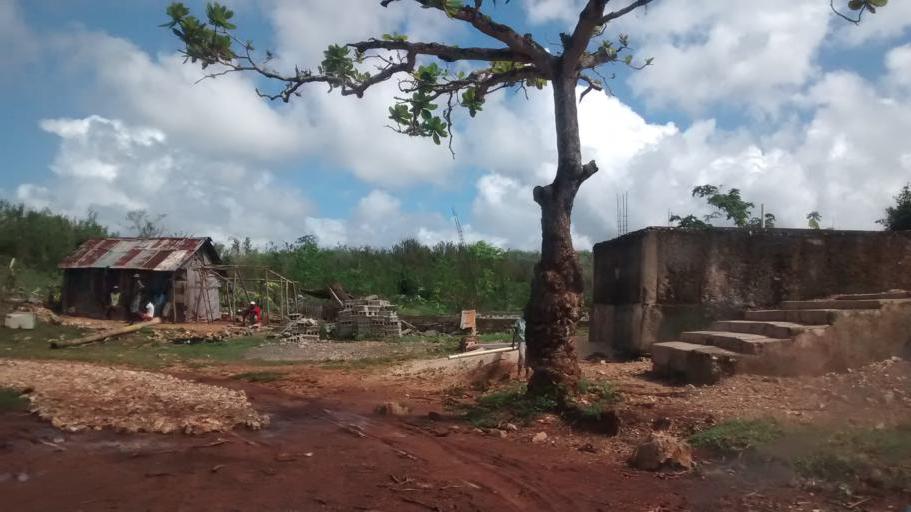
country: HT
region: Grandans
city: Corail
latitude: 18.5433
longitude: -73.9146
